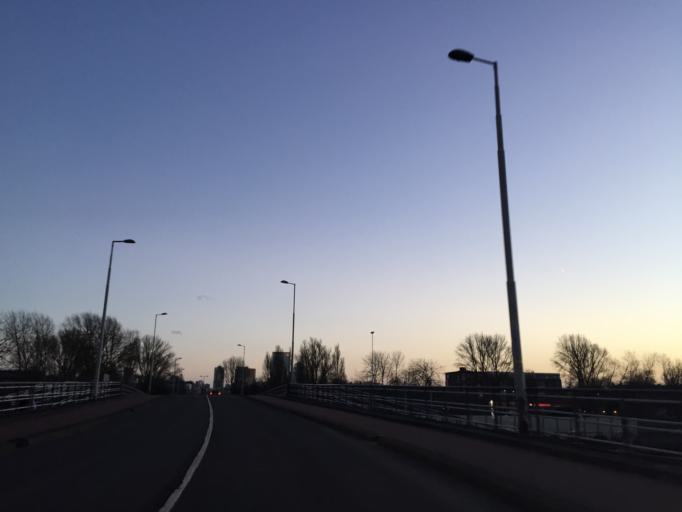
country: NL
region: South Holland
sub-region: Gemeente Rotterdam
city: Rotterdam
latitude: 51.9414
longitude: 4.4696
